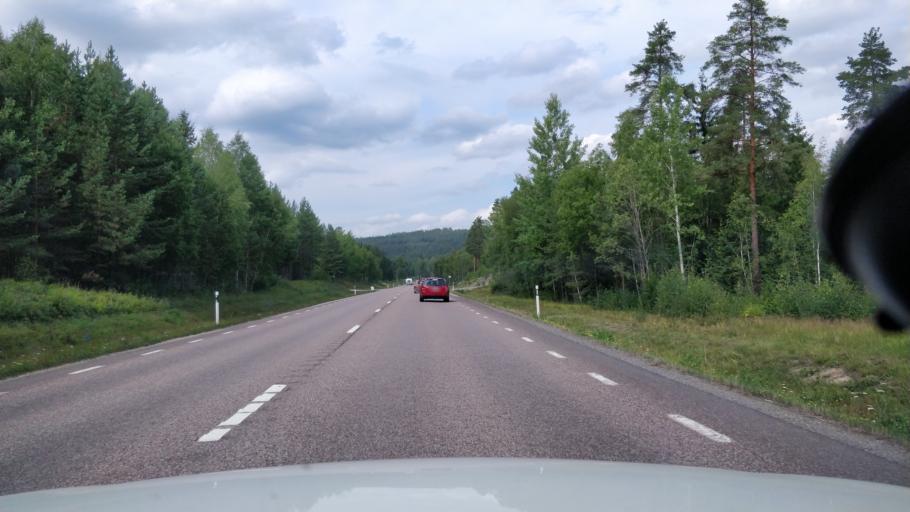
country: SE
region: Dalarna
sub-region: Faluns Kommun
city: Grycksbo
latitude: 60.6593
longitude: 15.5514
